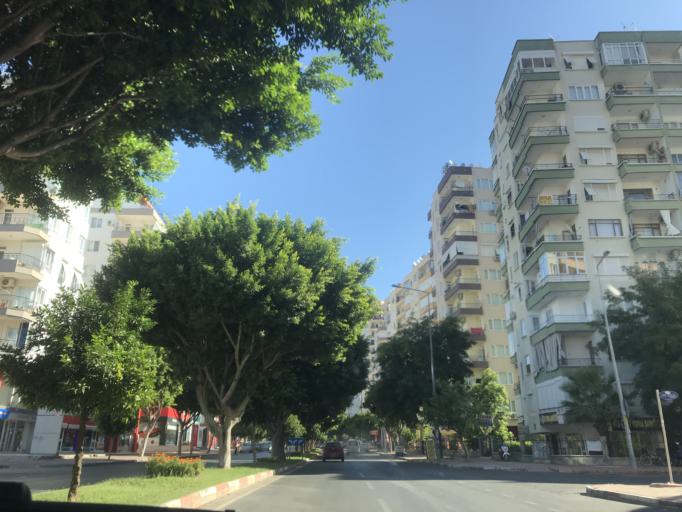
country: TR
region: Antalya
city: Antalya
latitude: 36.8970
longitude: 30.6295
